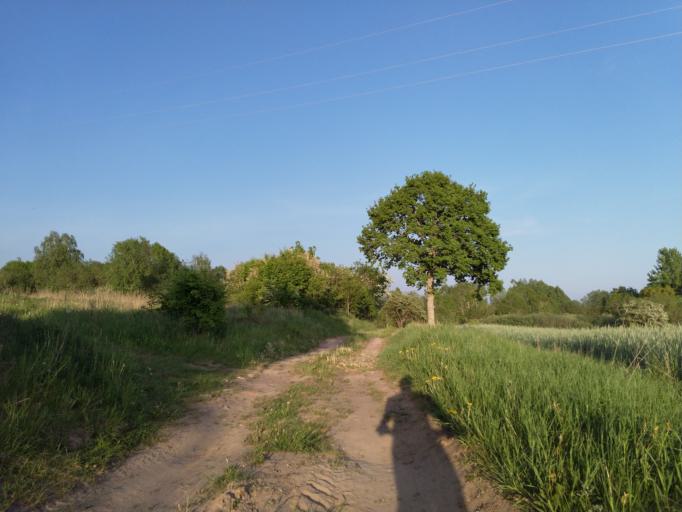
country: LV
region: Aizpute
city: Aizpute
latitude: 56.8324
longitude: 21.7803
